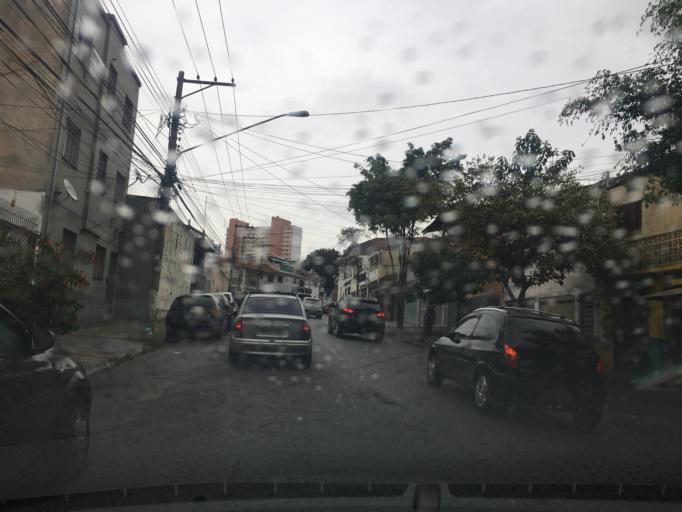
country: BR
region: Sao Paulo
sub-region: Guarulhos
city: Guarulhos
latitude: -23.5300
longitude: -46.5624
